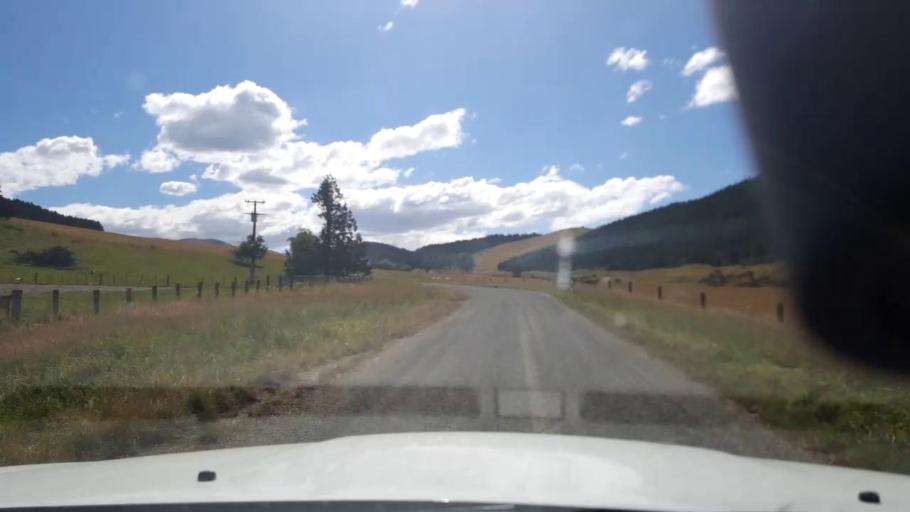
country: NZ
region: Canterbury
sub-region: Timaru District
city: Pleasant Point
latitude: -44.3127
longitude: 170.9199
